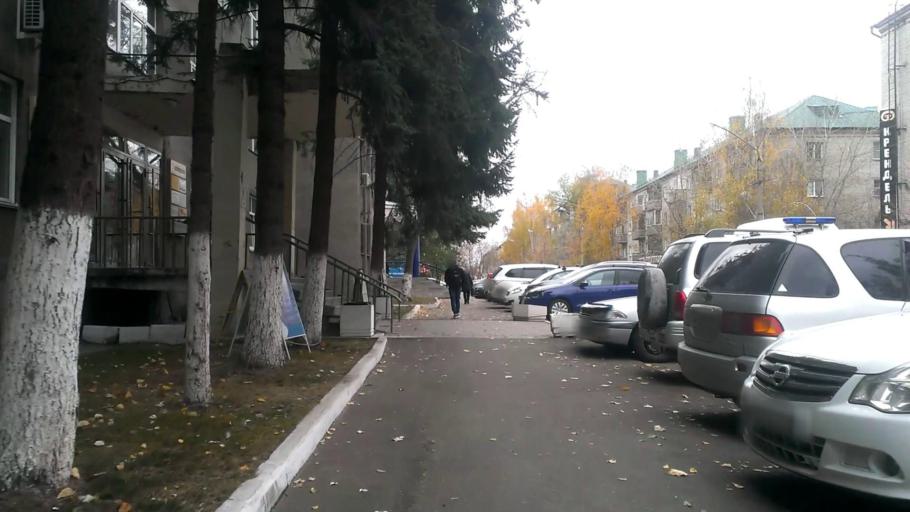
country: RU
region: Altai Krai
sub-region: Gorod Barnaulskiy
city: Barnaul
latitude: 53.3493
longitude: 83.7713
